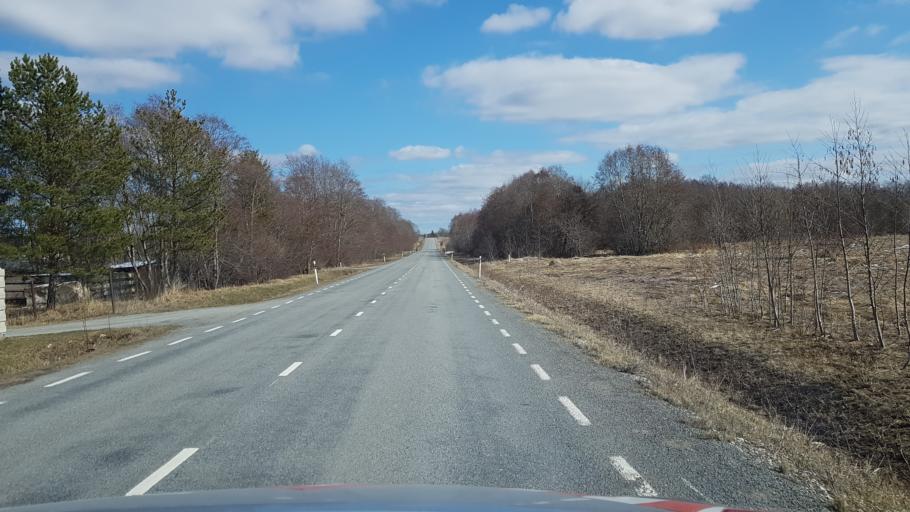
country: EE
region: Laeaene-Virumaa
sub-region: Tapa vald
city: Tapa
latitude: 59.2690
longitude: 25.9361
